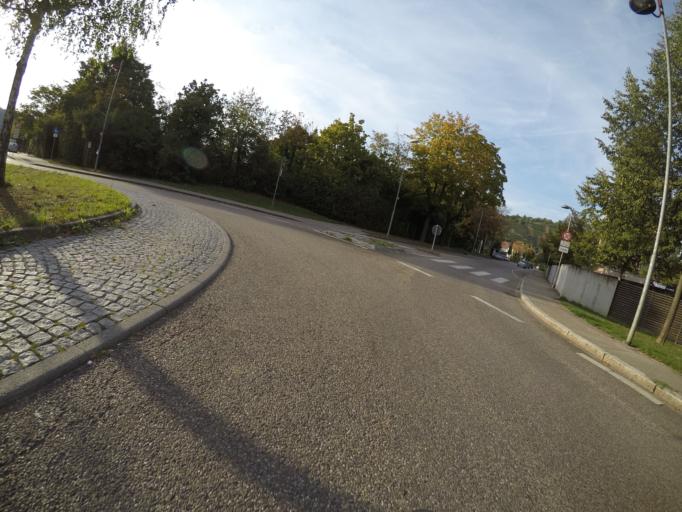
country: DE
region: Baden-Wuerttemberg
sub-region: Regierungsbezirk Stuttgart
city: Esslingen
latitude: 48.7357
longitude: 9.2902
